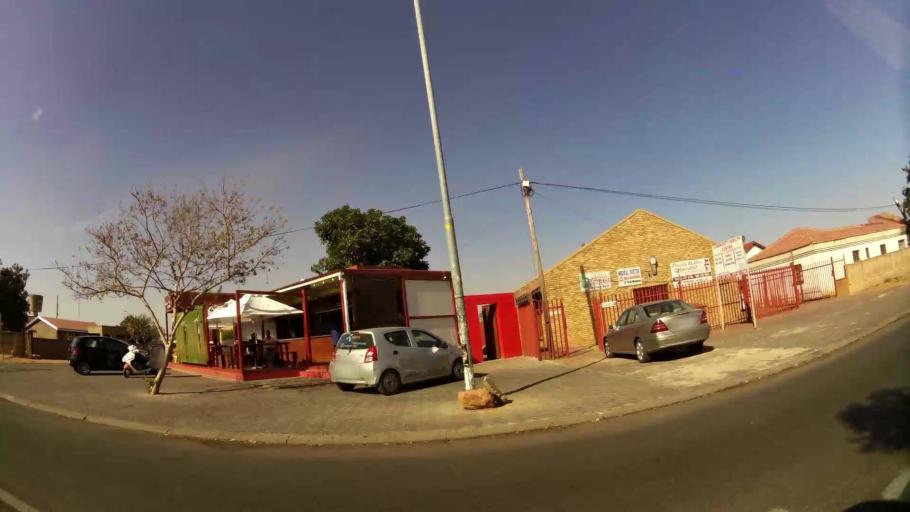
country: ZA
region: Gauteng
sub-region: City of Tshwane Metropolitan Municipality
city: Mabopane
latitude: -25.5385
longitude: 28.0990
